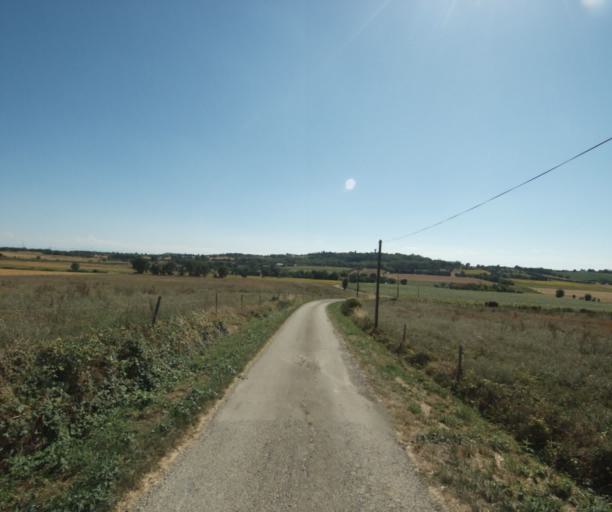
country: FR
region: Midi-Pyrenees
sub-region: Departement de la Haute-Garonne
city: Saint-Felix-Lauragais
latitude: 43.5005
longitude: 1.9136
